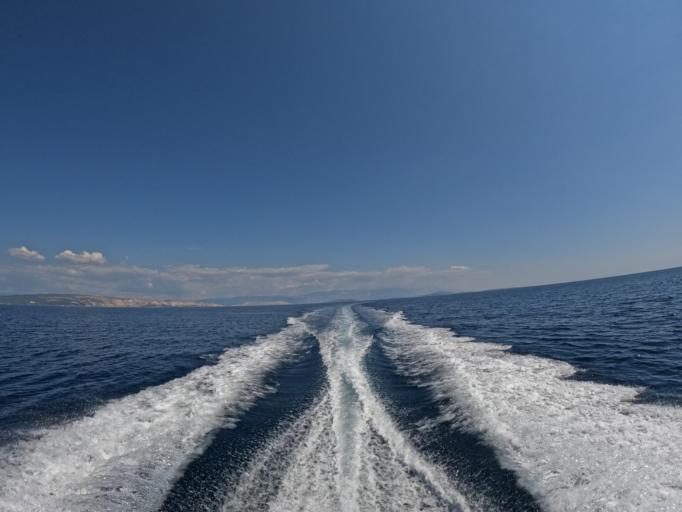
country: HR
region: Primorsko-Goranska
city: Cres
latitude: 44.9344
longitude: 14.5135
